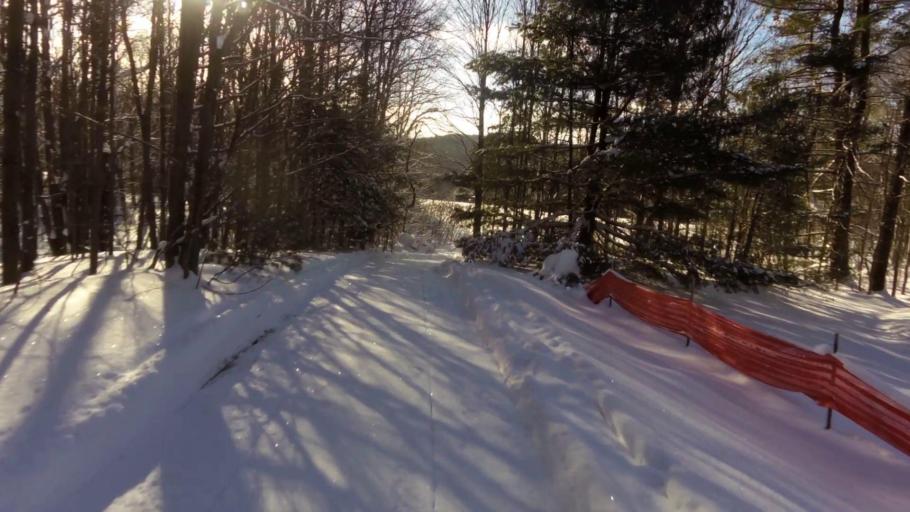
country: US
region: New York
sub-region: Chautauqua County
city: Falconer
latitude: 42.2570
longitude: -79.1712
